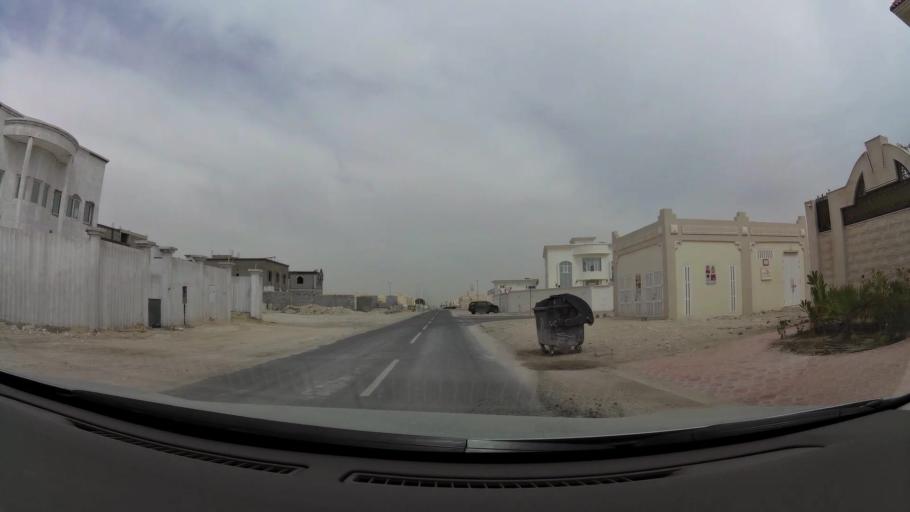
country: QA
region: Baladiyat ar Rayyan
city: Ar Rayyan
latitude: 25.2192
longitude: 51.4629
